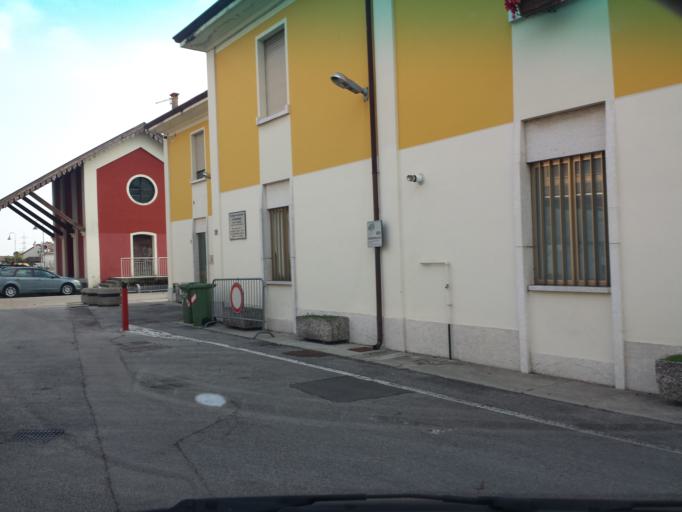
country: IT
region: Veneto
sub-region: Provincia di Vicenza
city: Dueville
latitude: 45.6352
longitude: 11.5464
